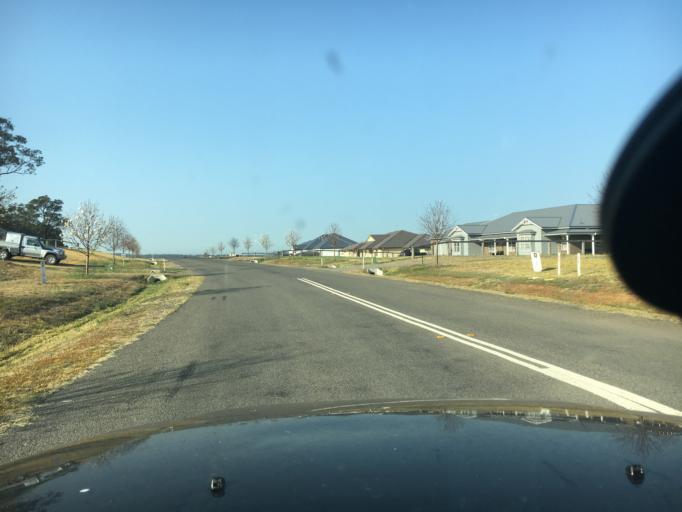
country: AU
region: New South Wales
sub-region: Cessnock
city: Branxton
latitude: -32.6392
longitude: 151.3585
